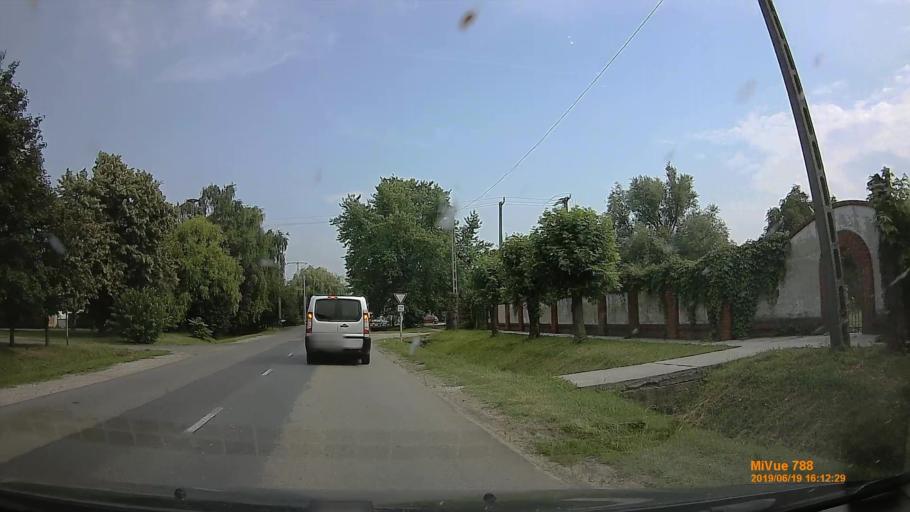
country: HU
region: Baranya
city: Szigetvar
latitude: 46.0495
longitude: 17.7846
